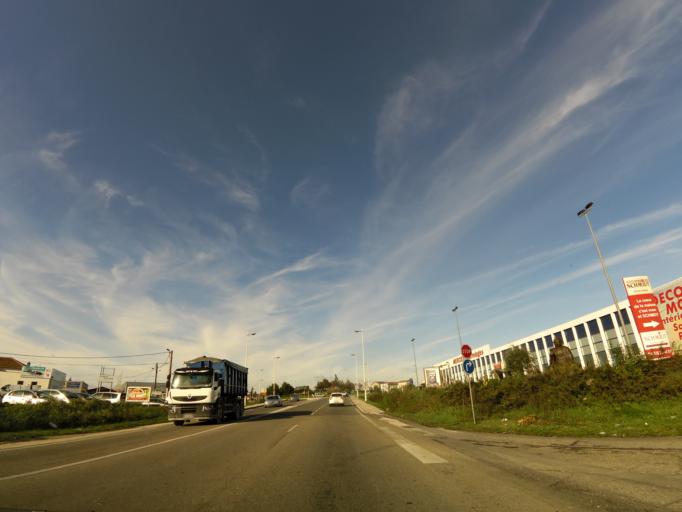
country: FR
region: Languedoc-Roussillon
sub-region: Departement du Gard
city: Ales
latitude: 44.1280
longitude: 4.1067
